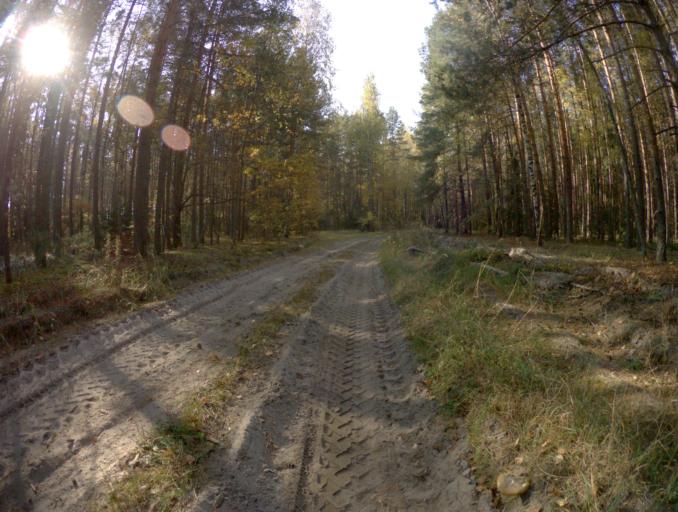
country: RU
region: Vladimir
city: Vorsha
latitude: 55.9525
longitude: 40.1387
